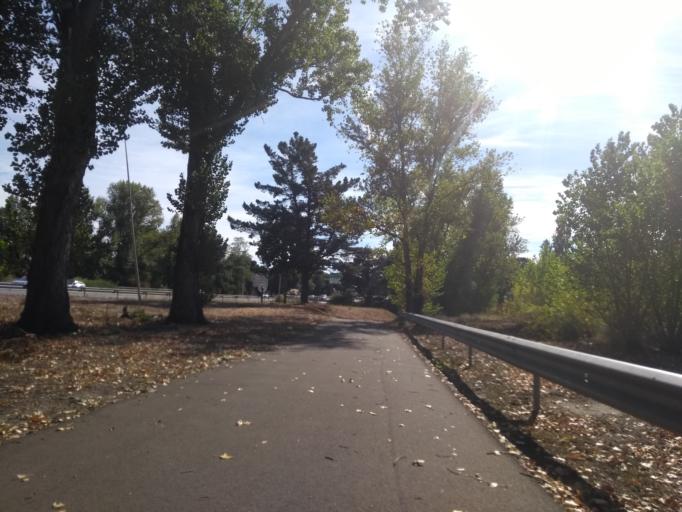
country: FR
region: Aquitaine
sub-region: Departement de la Gironde
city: Le Bouscat
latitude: 44.8875
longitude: -0.5606
